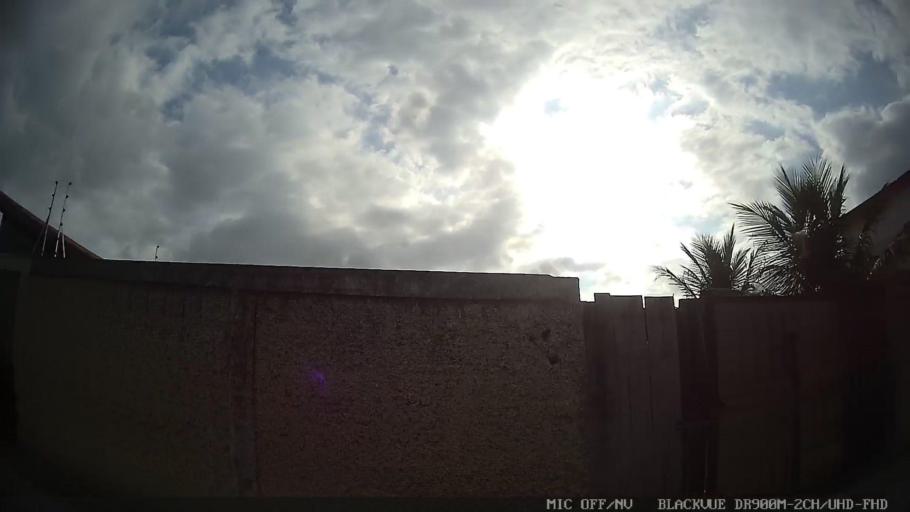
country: BR
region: Sao Paulo
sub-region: Itanhaem
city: Itanhaem
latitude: -24.1965
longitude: -46.8070
